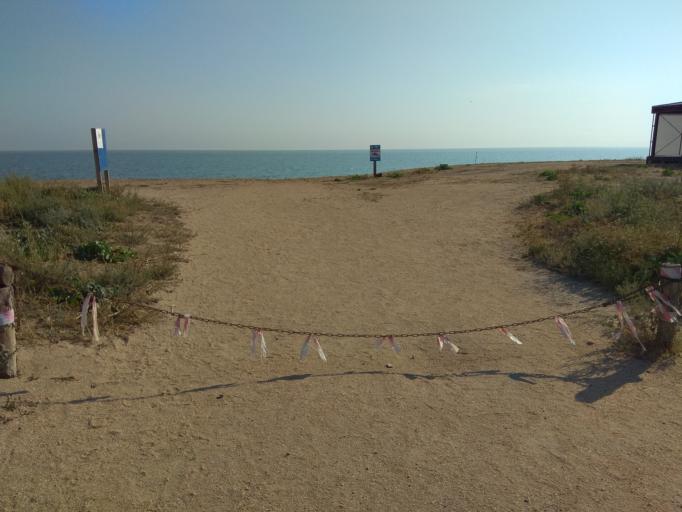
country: RU
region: Krasnodarskiy
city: Dolzhanskaya
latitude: 46.6820
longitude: 37.7383
